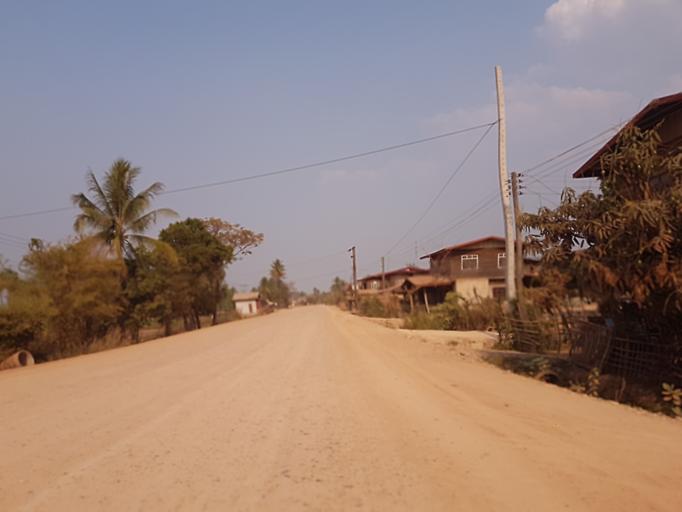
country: TH
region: Nong Khai
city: Nong Khai
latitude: 17.9831
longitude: 102.8899
